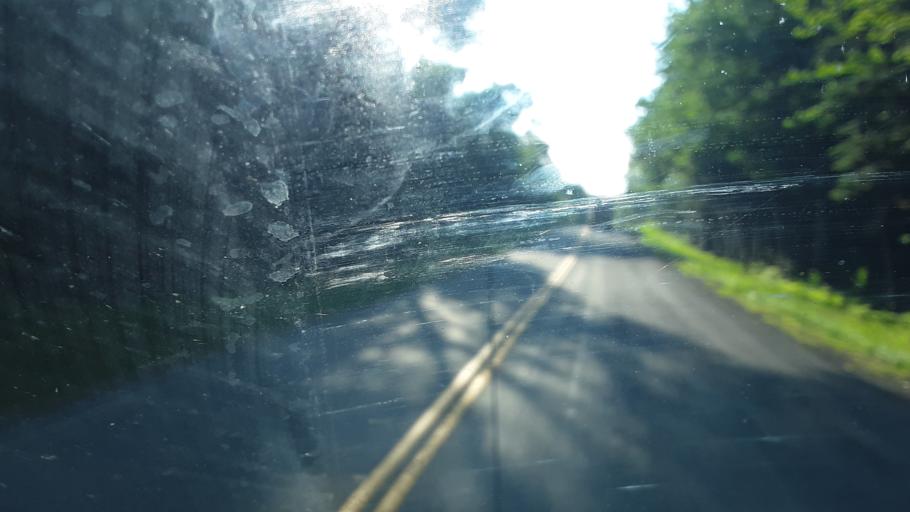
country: US
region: Maine
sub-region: Penobscot County
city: Patten
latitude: 46.2021
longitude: -68.2839
